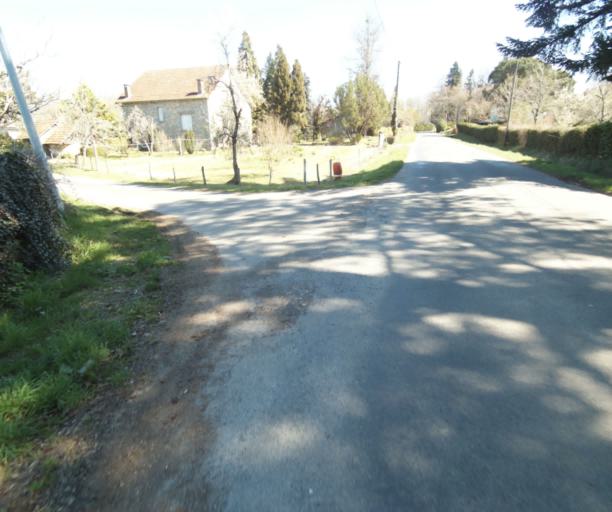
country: FR
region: Limousin
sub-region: Departement de la Correze
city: Saint-Mexant
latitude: 45.3222
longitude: 1.6490
